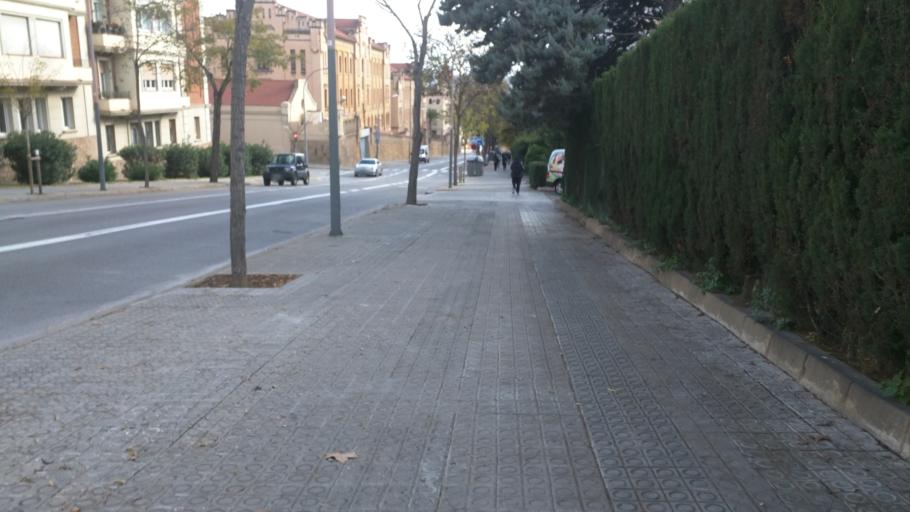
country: ES
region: Catalonia
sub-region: Provincia de Barcelona
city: Esplugues de Llobregat
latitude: 41.3865
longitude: 2.1073
